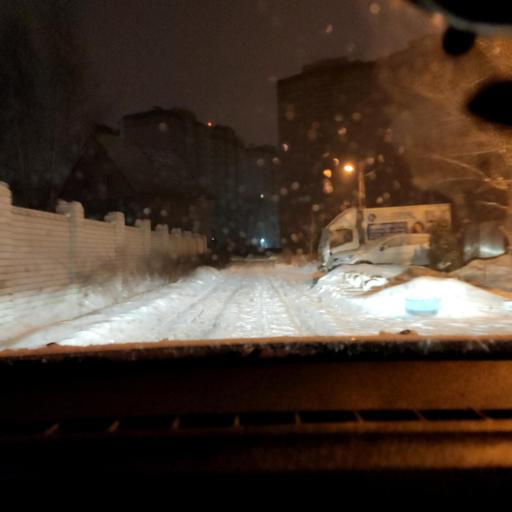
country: RU
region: Voronezj
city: Podgornoye
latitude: 51.7339
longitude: 39.1884
